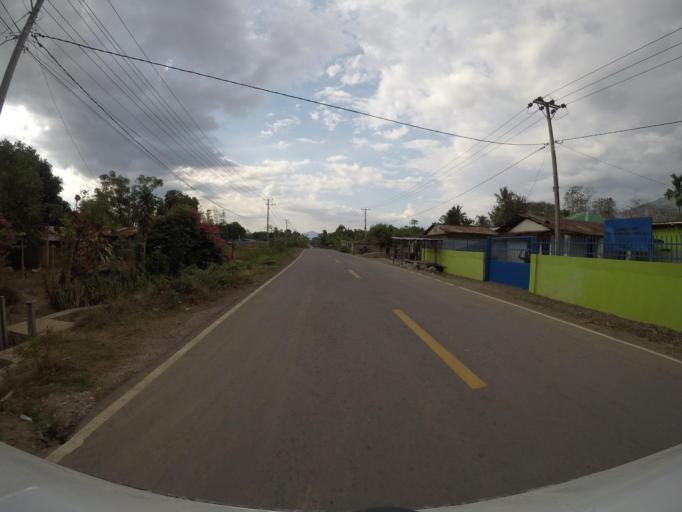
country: TL
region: Bobonaro
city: Maliana
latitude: -8.9731
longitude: 125.2192
